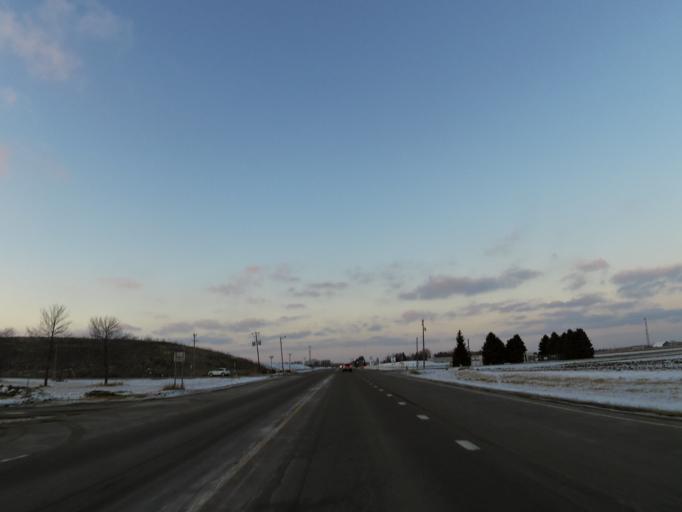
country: US
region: Minnesota
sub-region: Dakota County
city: Rosemount
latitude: 44.7019
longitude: -93.1366
